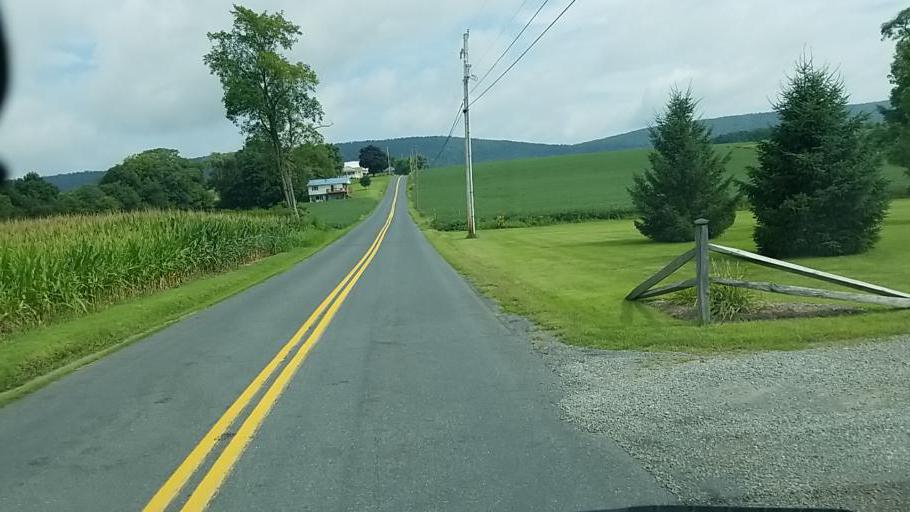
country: US
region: Pennsylvania
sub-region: Dauphin County
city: Matamoras
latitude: 40.5042
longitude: -76.8853
